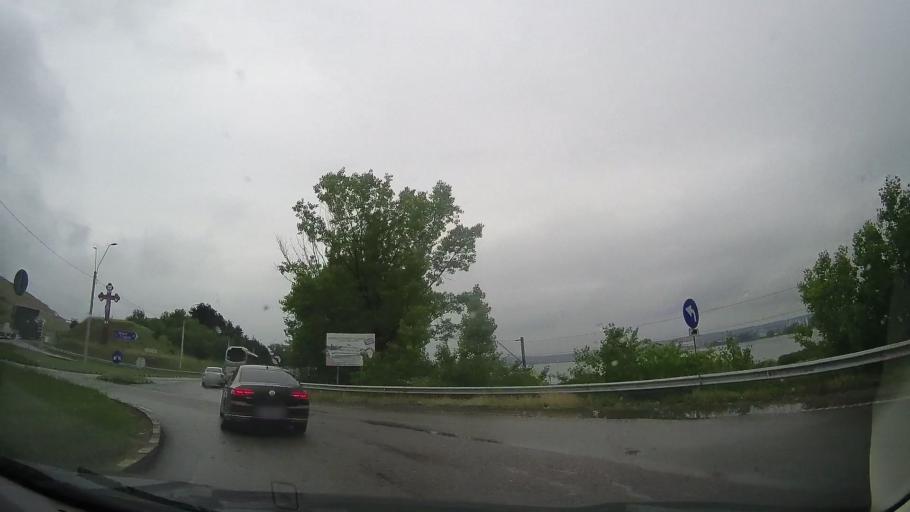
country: RS
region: Central Serbia
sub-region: Borski Okrug
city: Kladovo
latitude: 44.6346
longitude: 22.5890
